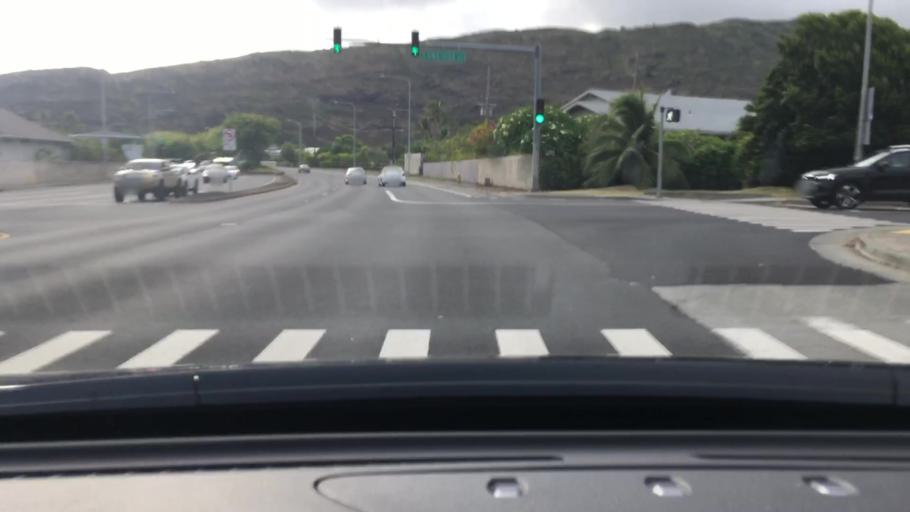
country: US
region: Hawaii
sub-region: Honolulu County
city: Waimanalo Beach
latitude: 21.2859
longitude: -157.7194
